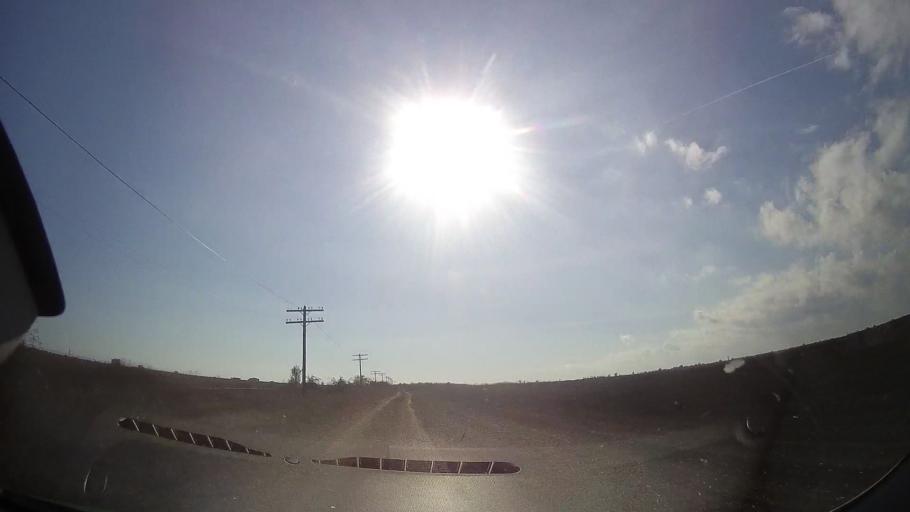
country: RO
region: Constanta
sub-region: Comuna Tuzla
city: Tuzla
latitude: 43.9795
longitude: 28.6443
